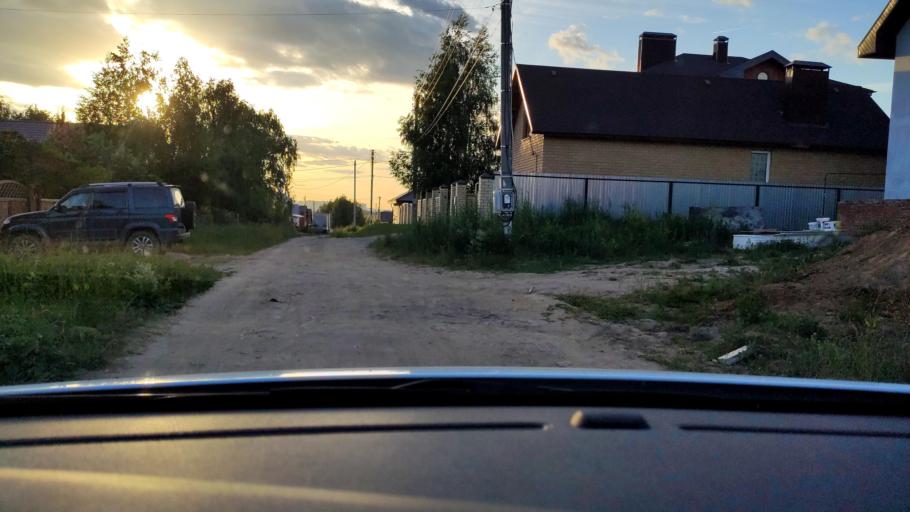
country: RU
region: Tatarstan
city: Stolbishchi
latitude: 55.7576
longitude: 49.2818
